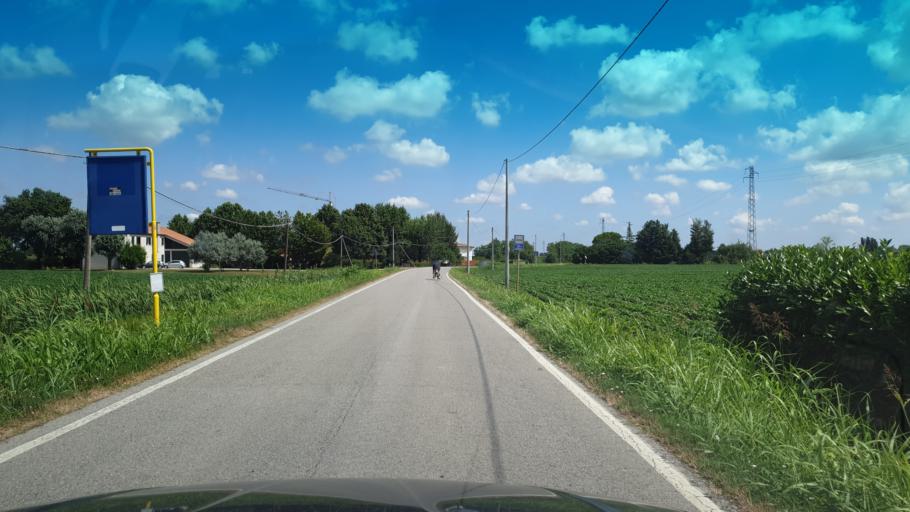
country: IT
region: Veneto
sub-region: Provincia di Rovigo
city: Costa di Rovigo
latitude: 45.0658
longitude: 11.7146
